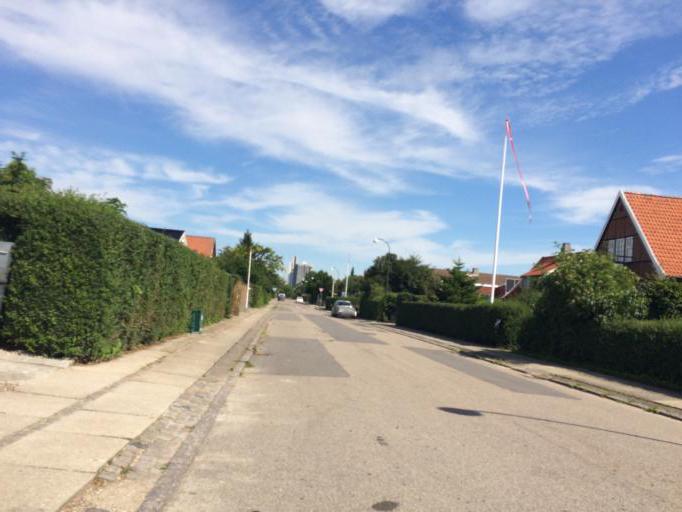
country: DK
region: Capital Region
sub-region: Herlev Kommune
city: Herlev
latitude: 55.7152
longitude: 12.4426
